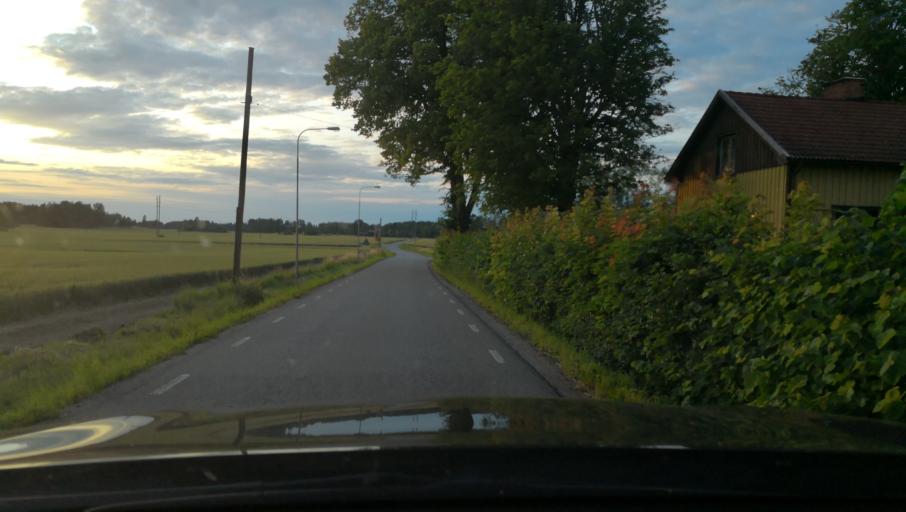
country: SE
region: Uppsala
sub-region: Uppsala Kommun
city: Vattholma
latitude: 60.0392
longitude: 17.6646
